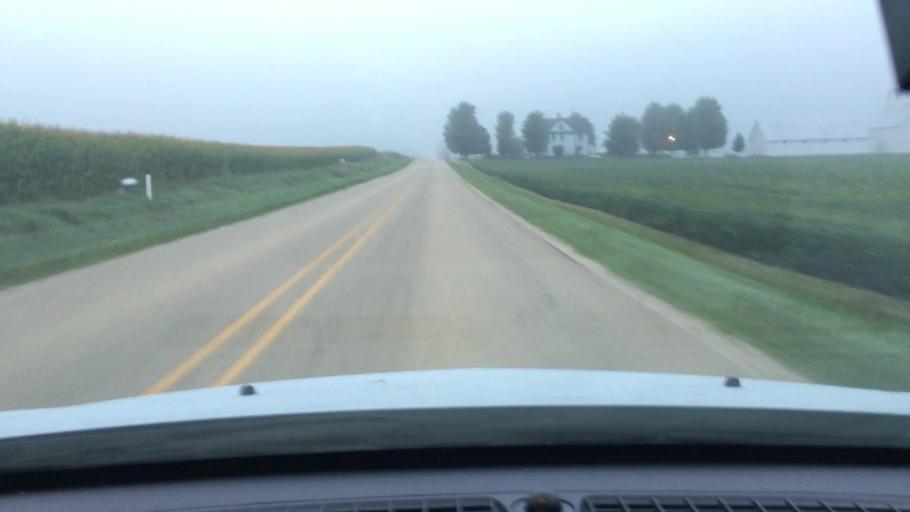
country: US
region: Illinois
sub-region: DeKalb County
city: Malta
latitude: 41.8862
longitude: -88.9616
